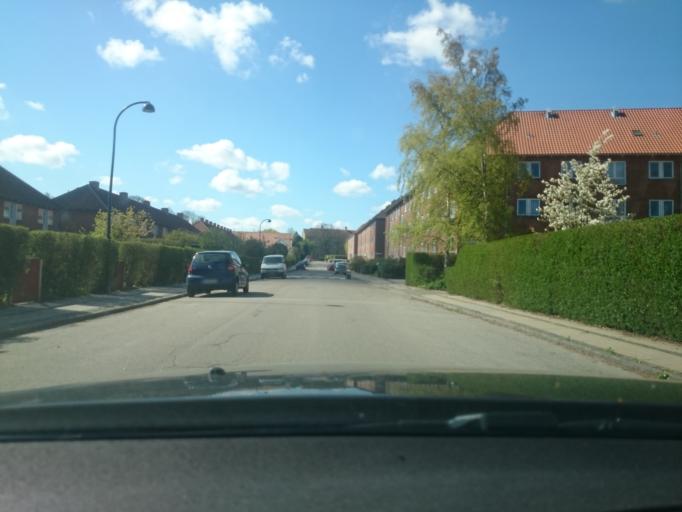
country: DK
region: Capital Region
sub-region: Lyngby-Tarbaek Kommune
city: Kongens Lyngby
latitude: 55.7531
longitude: 12.5151
